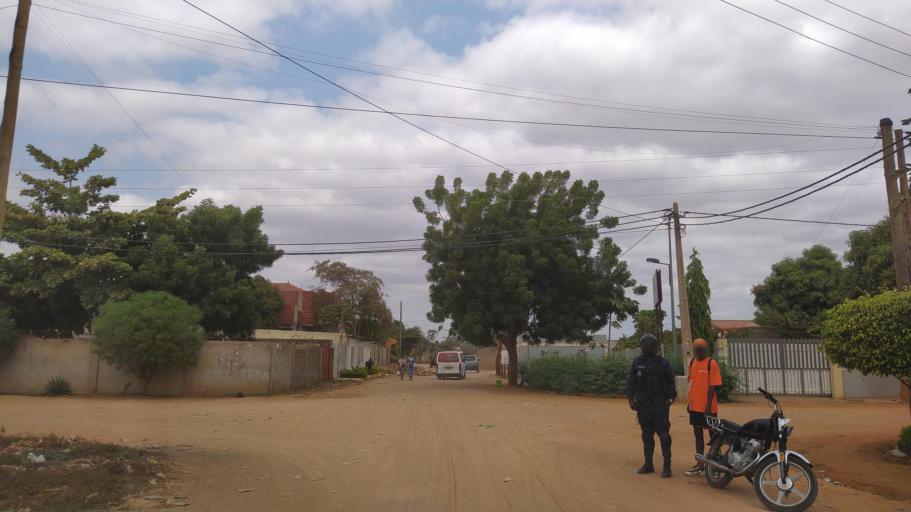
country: AO
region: Luanda
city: Luanda
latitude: -8.9288
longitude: 13.2615
